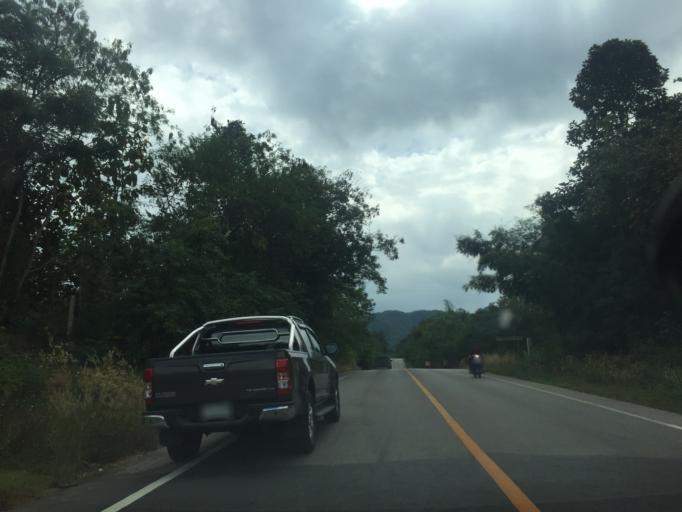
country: TH
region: Lampang
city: Mueang Pan
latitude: 18.7853
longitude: 99.5219
